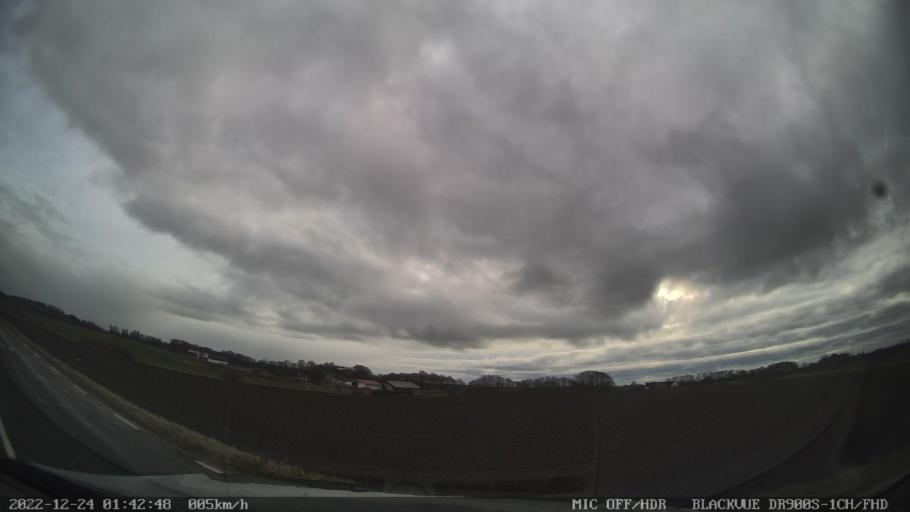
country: SE
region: Skane
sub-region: Tomelilla Kommun
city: Tomelilla
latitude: 55.5999
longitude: 14.0735
